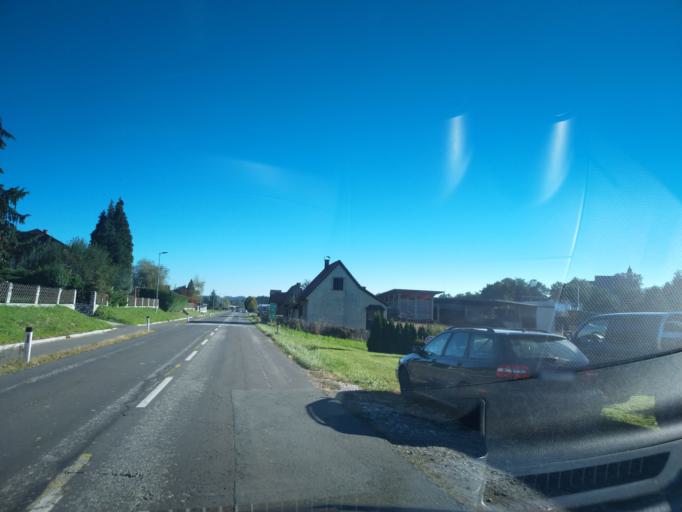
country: AT
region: Styria
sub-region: Politischer Bezirk Deutschlandsberg
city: Stainz
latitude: 46.9038
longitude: 15.2654
